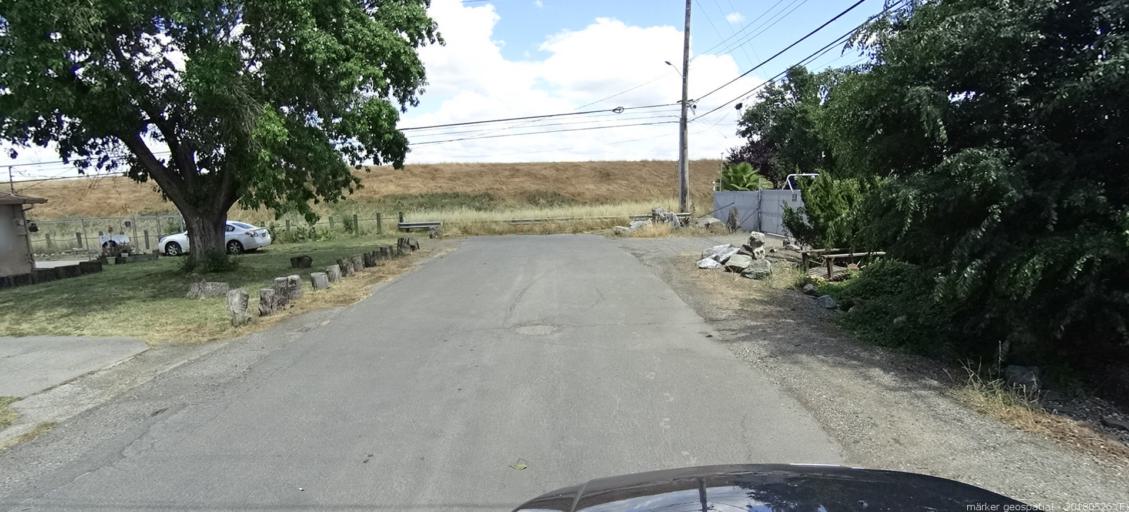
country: US
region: California
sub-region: Sacramento County
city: Sacramento
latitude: 38.6335
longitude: -121.4723
